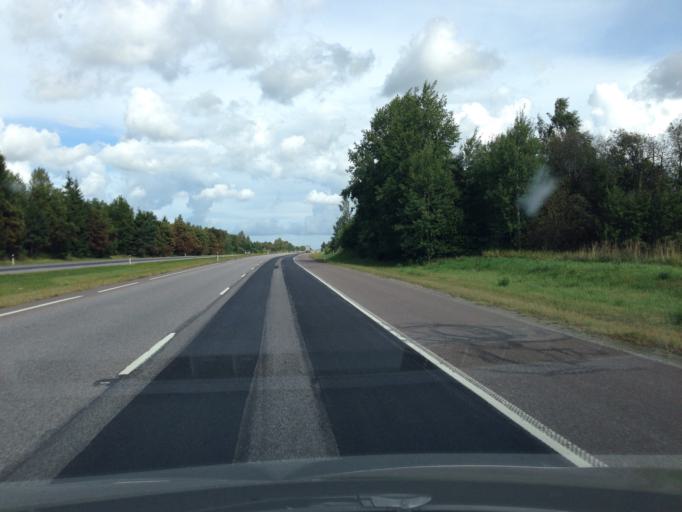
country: EE
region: Harju
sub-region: Saue linn
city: Saue
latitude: 59.2868
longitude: 24.5370
